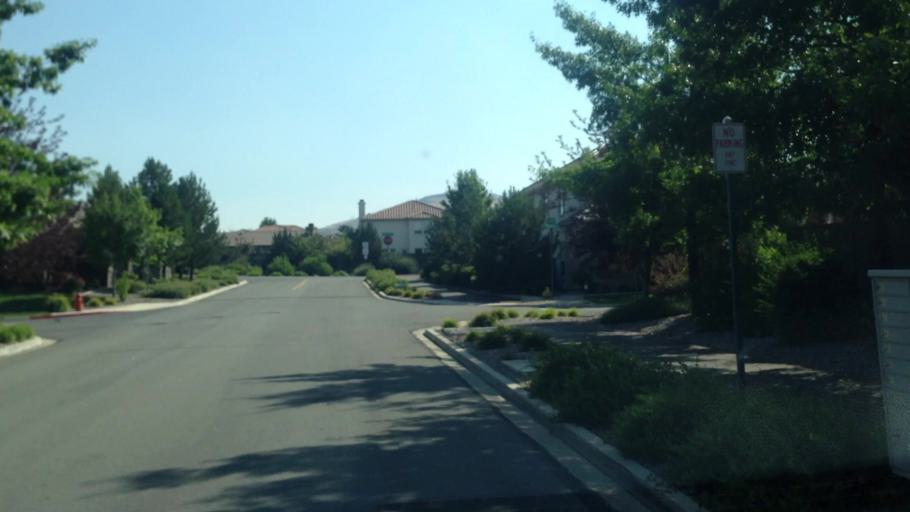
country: US
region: Nevada
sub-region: Storey County
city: Virginia City
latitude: 39.4032
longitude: -119.7336
